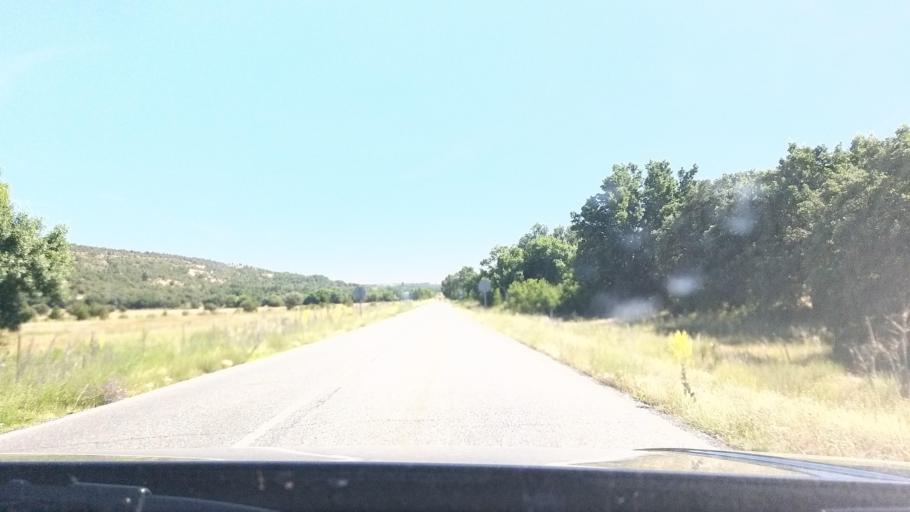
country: ES
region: Castille and Leon
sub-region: Provincia de Segovia
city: Arahuetes
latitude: 41.1268
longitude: -3.8411
